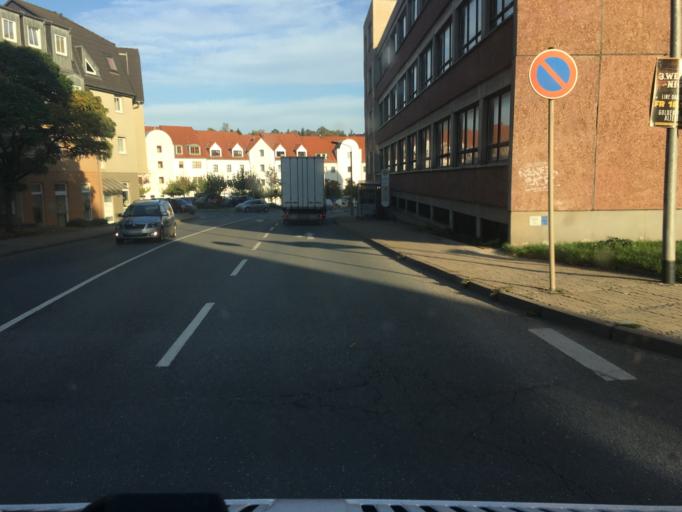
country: DE
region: Saxony
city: Werdau
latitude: 50.7377
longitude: 12.3774
